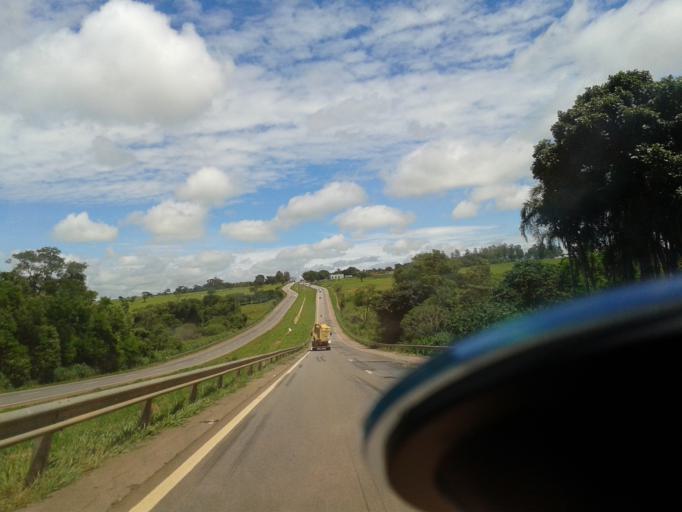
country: BR
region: Goias
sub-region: Inhumas
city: Inhumas
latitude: -16.2790
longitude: -49.5425
